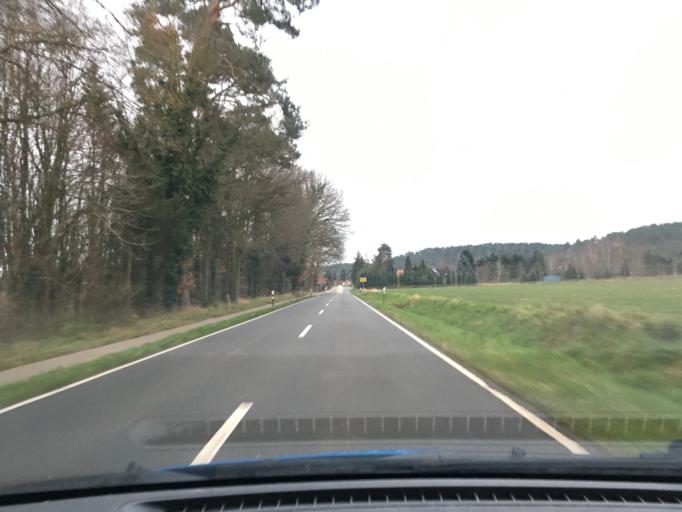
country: DE
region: Lower Saxony
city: Tosterglope
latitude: 53.2416
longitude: 10.8396
